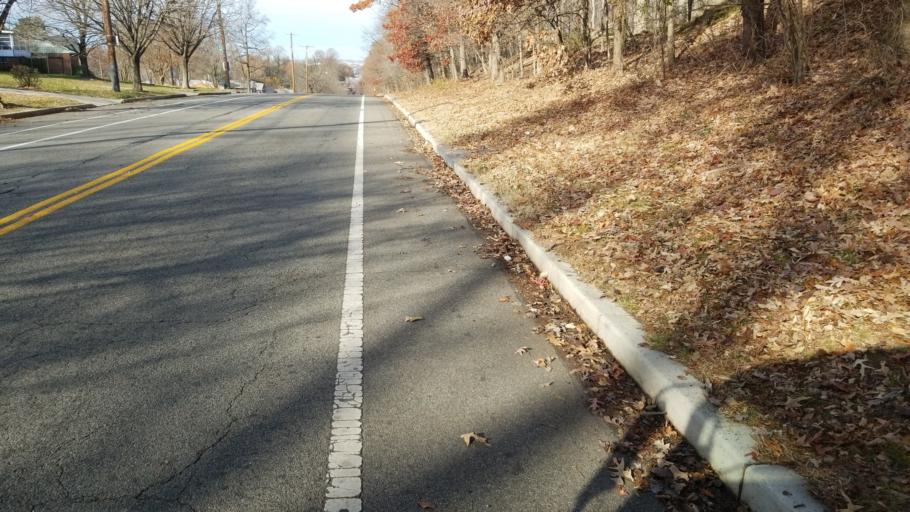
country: US
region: Maryland
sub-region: Prince George's County
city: Coral Hills
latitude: 38.8746
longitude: -76.9530
